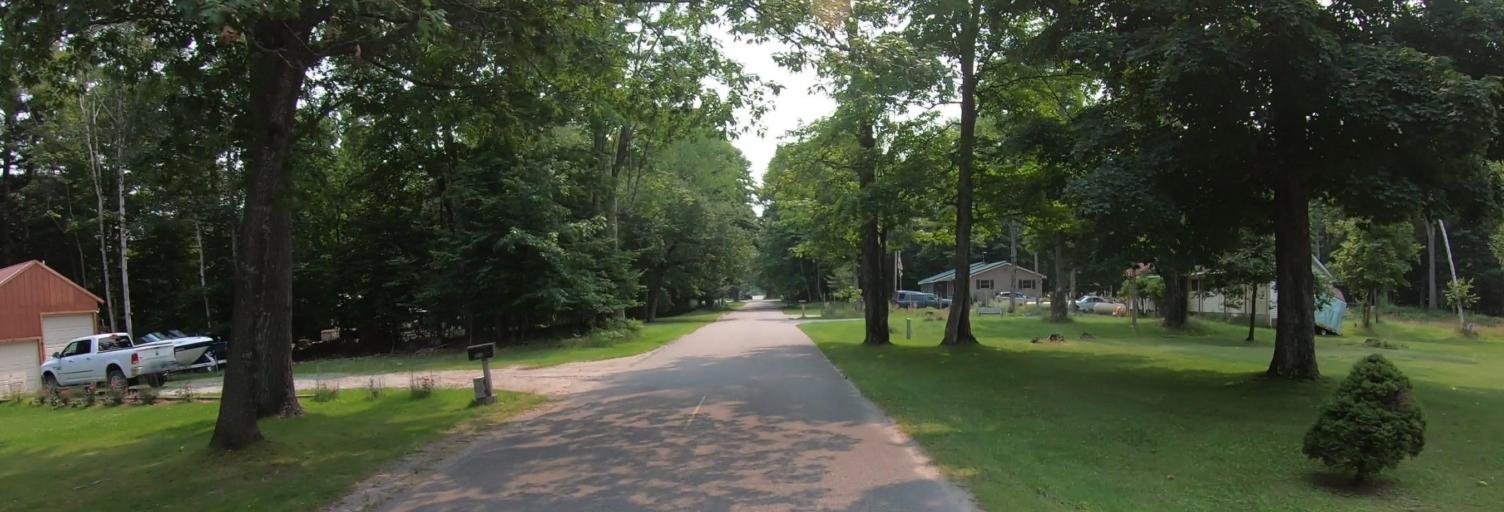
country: CA
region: Ontario
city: Thessalon
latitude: 46.0182
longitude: -83.7436
